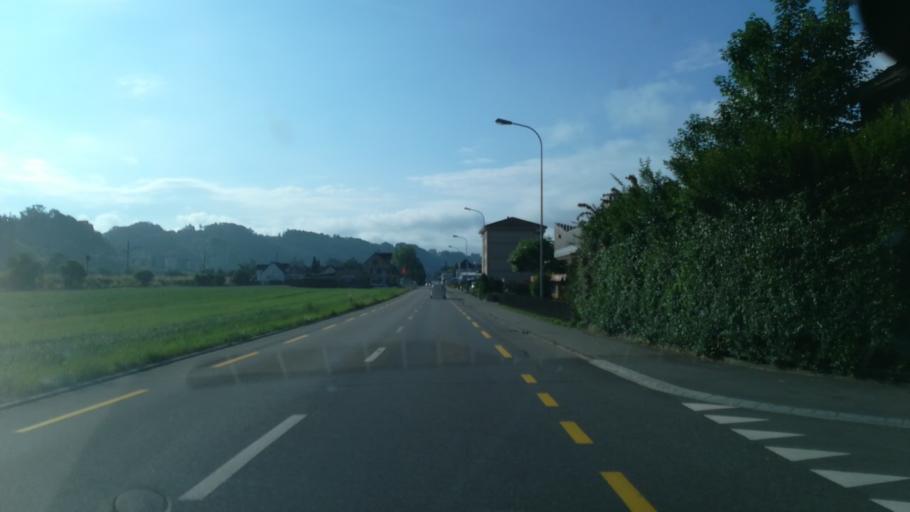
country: CH
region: Thurgau
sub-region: Weinfelden District
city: Sulgen
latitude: 47.5308
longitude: 9.1909
